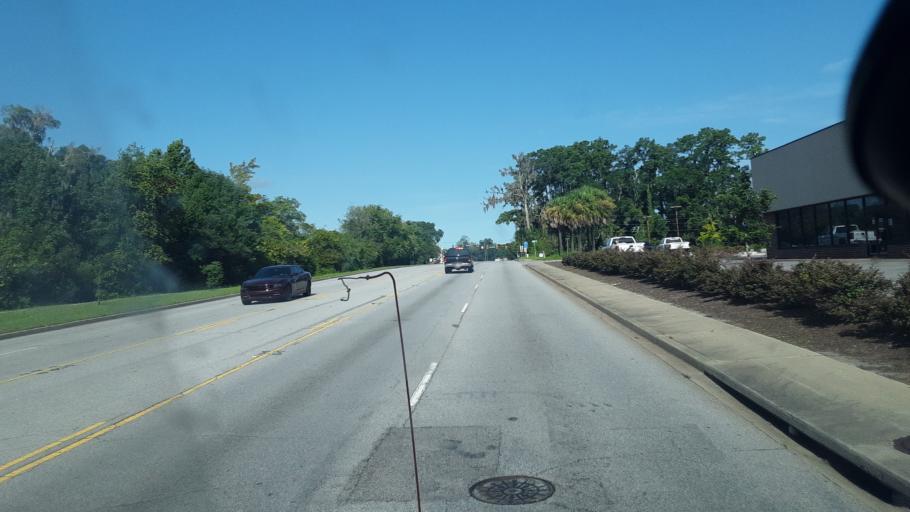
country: US
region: South Carolina
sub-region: Beaufort County
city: Burton
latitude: 32.4410
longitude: -80.7184
